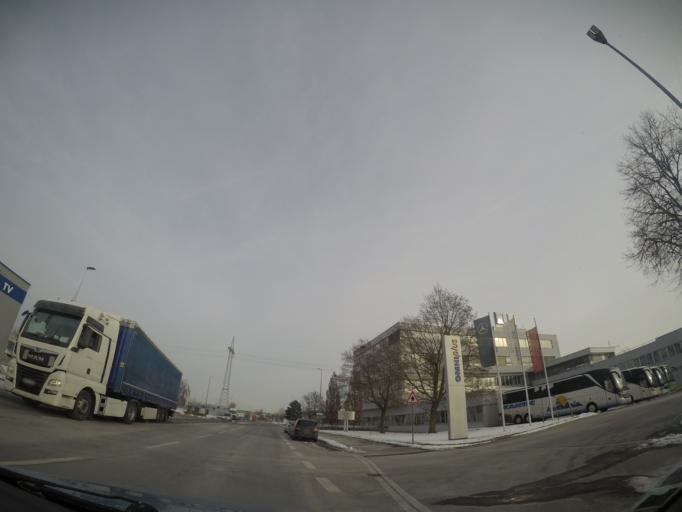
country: DE
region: Bavaria
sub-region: Swabia
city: Neu-Ulm
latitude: 48.3881
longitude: 10.0363
